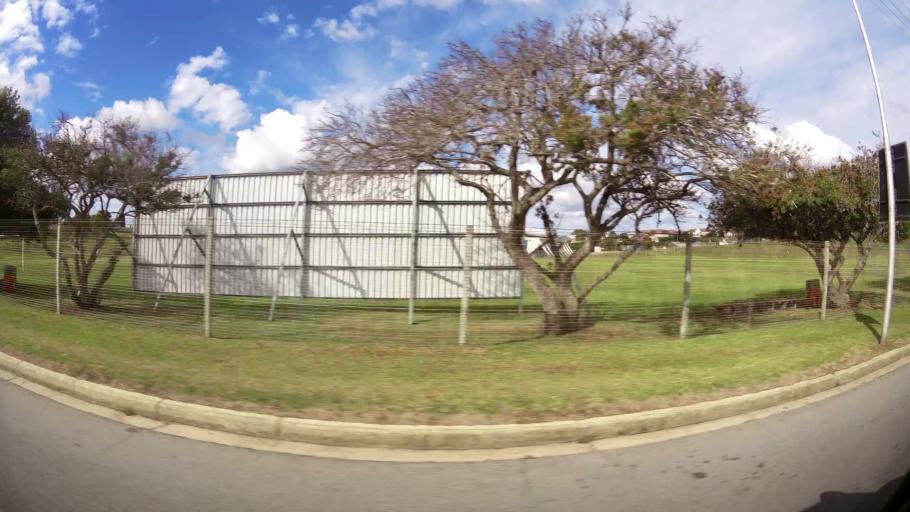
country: ZA
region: Eastern Cape
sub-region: Nelson Mandela Bay Metropolitan Municipality
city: Port Elizabeth
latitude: -33.9438
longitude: 25.5702
